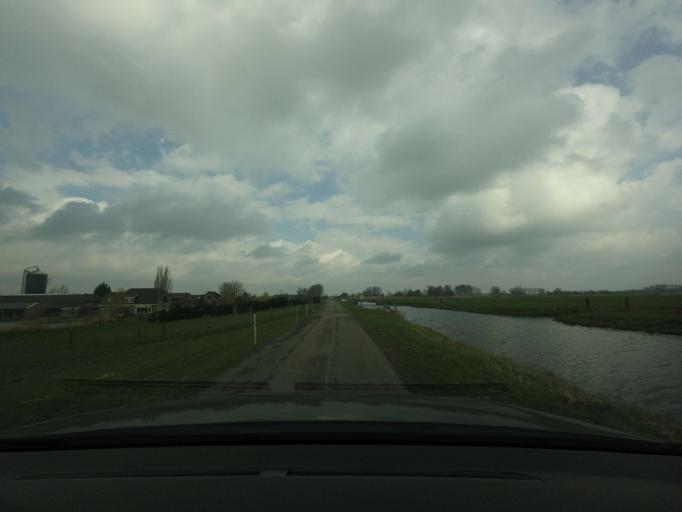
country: NL
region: North Holland
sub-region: Gemeente Uithoorn
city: Uithoorn
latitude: 52.2005
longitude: 4.8031
